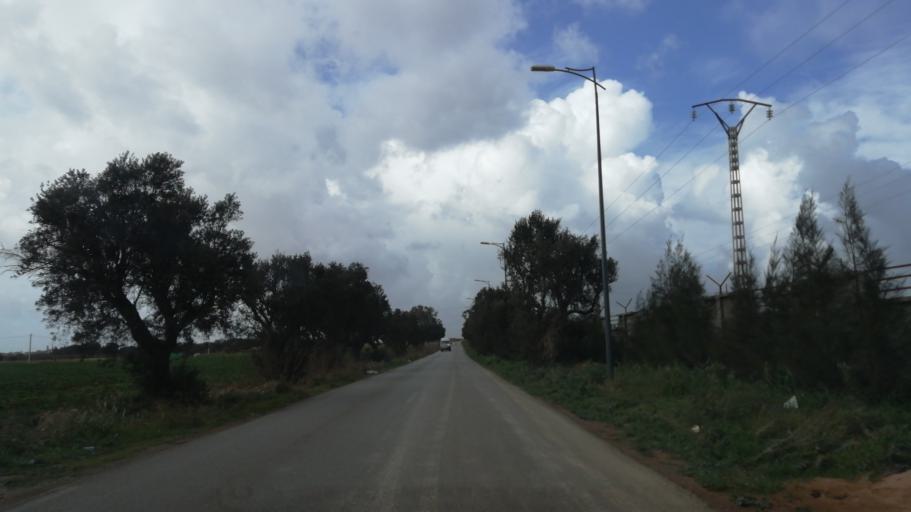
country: DZ
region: Oran
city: Sidi ech Chahmi
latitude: 35.6224
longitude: -0.5633
